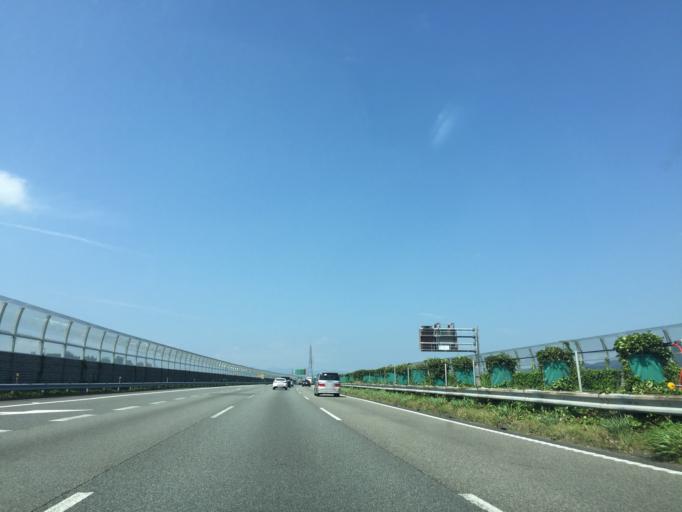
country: JP
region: Shizuoka
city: Gotemba
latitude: 35.2822
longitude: 138.9230
